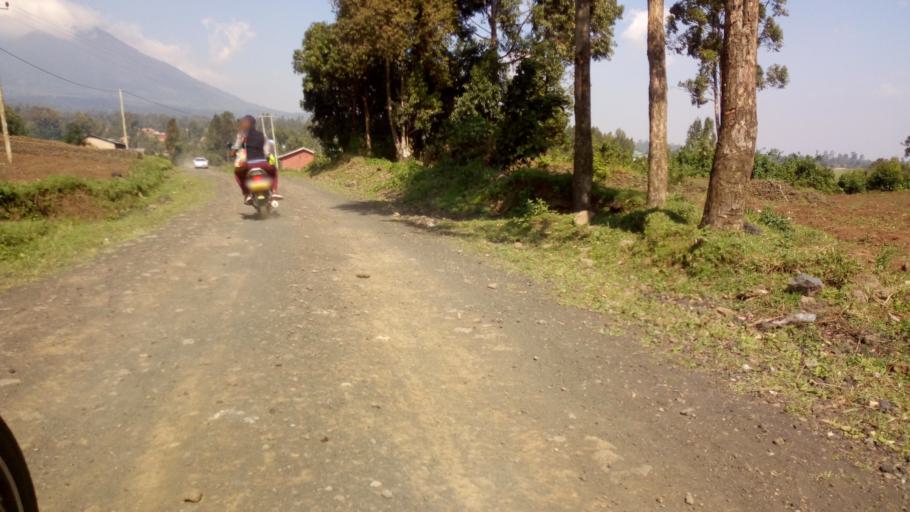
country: UG
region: Western Region
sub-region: Kisoro District
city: Kisoro
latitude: -1.3412
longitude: 29.6311
